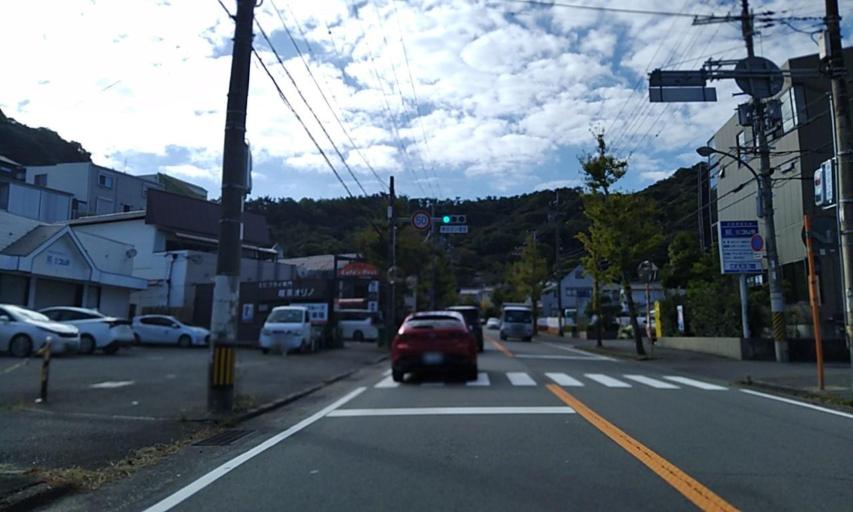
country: JP
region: Wakayama
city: Minato
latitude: 34.1934
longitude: 135.1590
